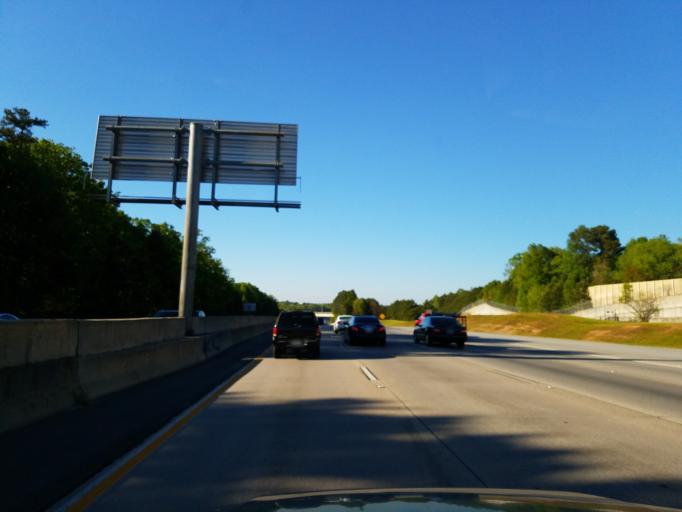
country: US
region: Georgia
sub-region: DeKalb County
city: Dunwoody
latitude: 33.9391
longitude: -84.3578
